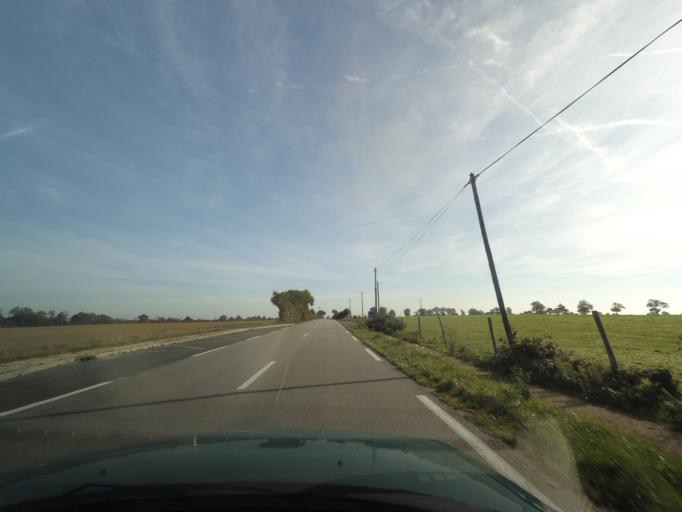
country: FR
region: Pays de la Loire
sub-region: Departement de la Vendee
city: Tiffauges
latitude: 47.0056
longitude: -1.1435
